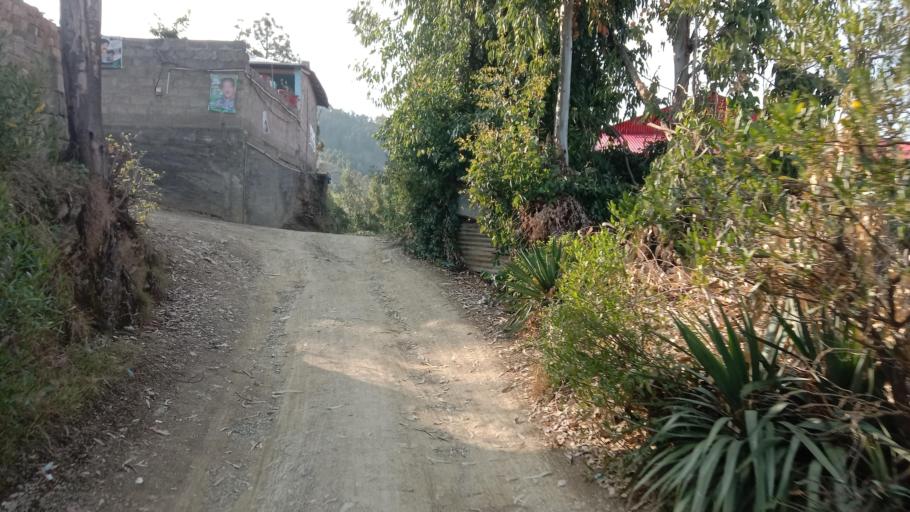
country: PK
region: Khyber Pakhtunkhwa
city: Abbottabad
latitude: 34.2048
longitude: 73.2066
